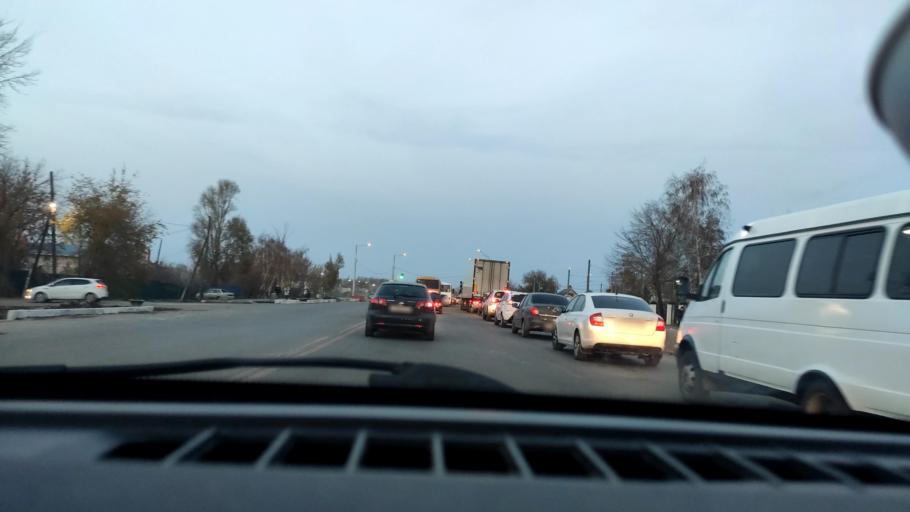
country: RU
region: Samara
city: Samara
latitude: 53.1317
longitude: 50.0959
